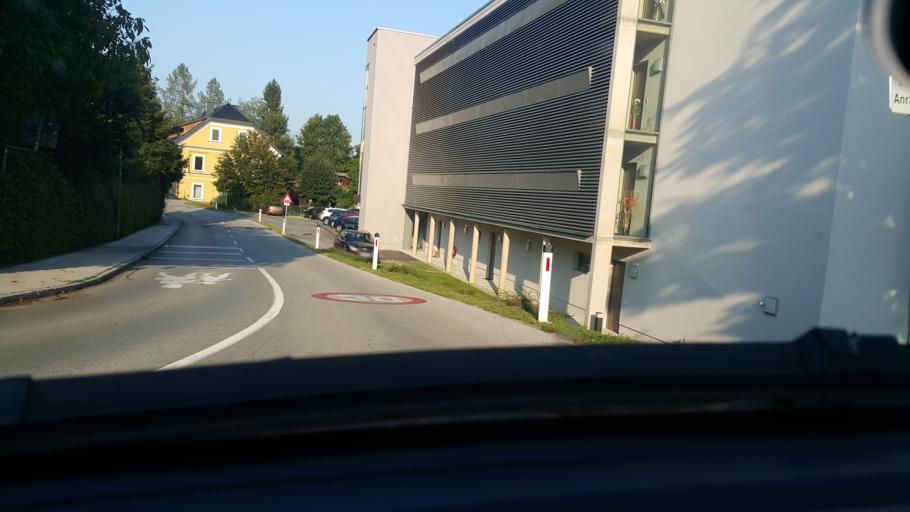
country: AT
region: Carinthia
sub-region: Politischer Bezirk Feldkirchen
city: Feldkirchen in Karnten
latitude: 46.7210
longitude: 14.0909
